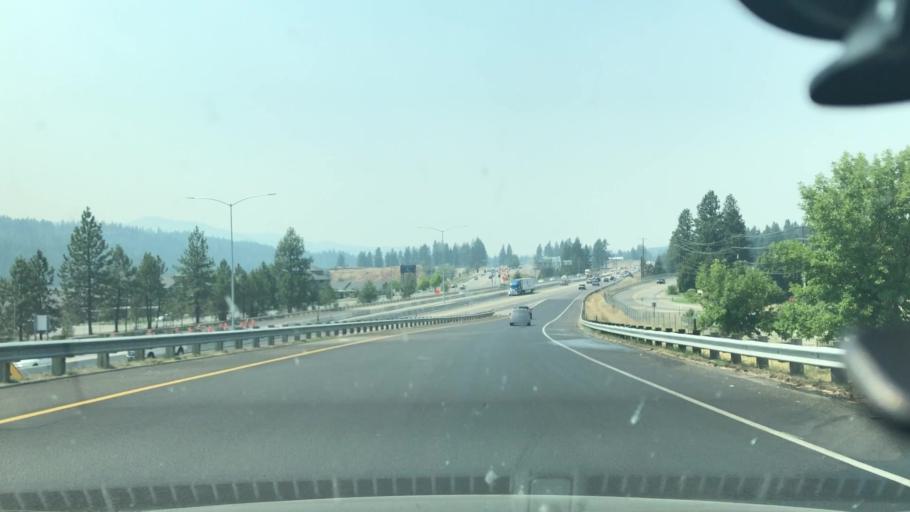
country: US
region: Idaho
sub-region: Kootenai County
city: Coeur d'Alene
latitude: 47.7006
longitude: -116.8097
